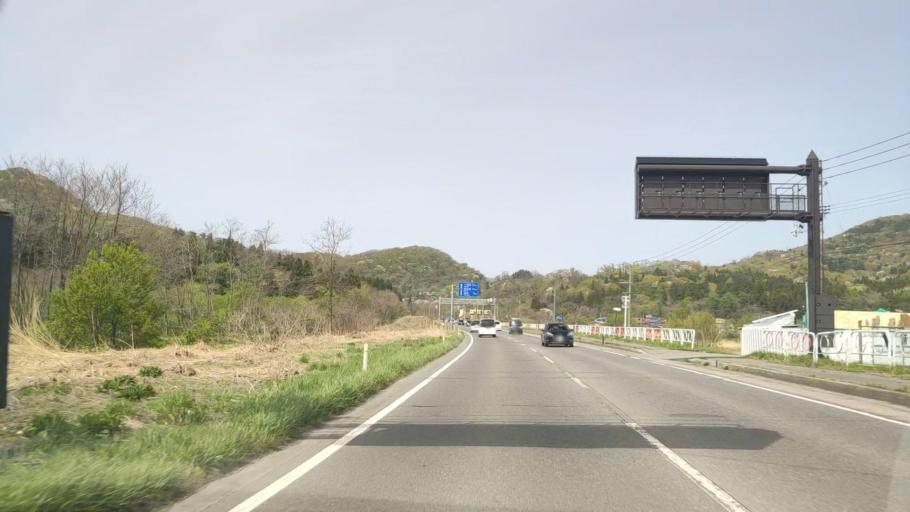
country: JP
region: Aomori
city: Aomori Shi
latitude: 40.8495
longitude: 140.8378
